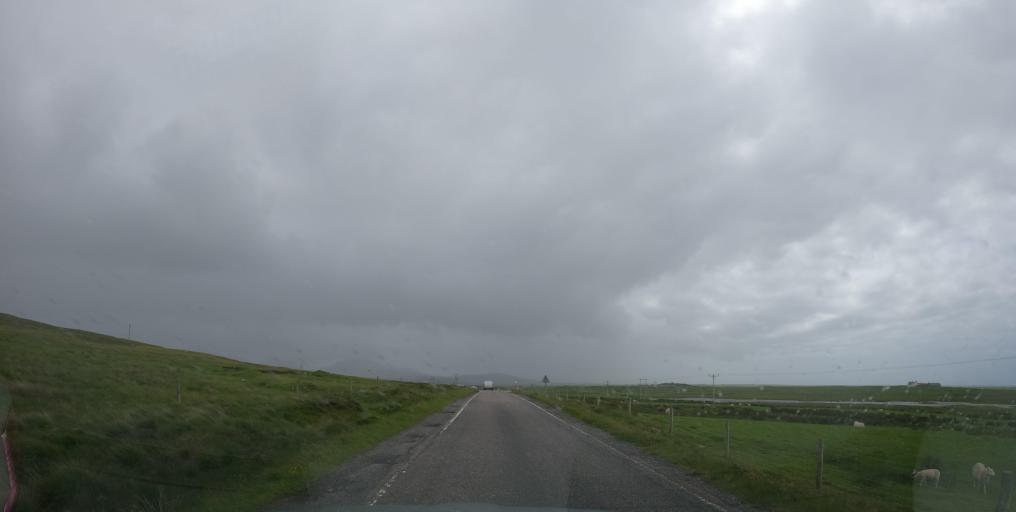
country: GB
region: Scotland
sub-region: Eilean Siar
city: Isle of South Uist
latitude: 57.3423
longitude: -7.3648
